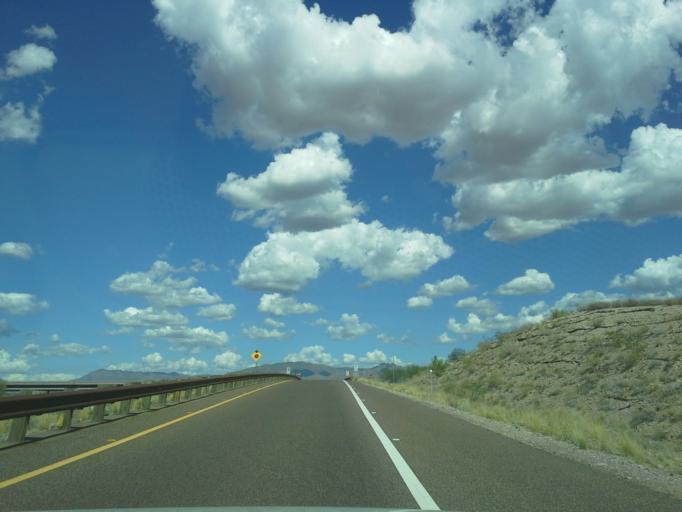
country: US
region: Arizona
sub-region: Maricopa County
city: Rio Verde
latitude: 33.6258
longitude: -111.5606
